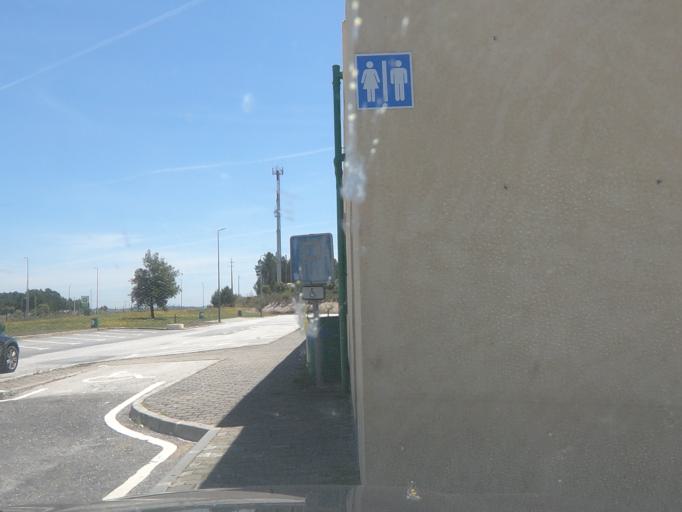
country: ES
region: Castille and Leon
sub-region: Provincia de Salamanca
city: Fuentes de Onoro
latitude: 40.6038
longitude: -6.9535
